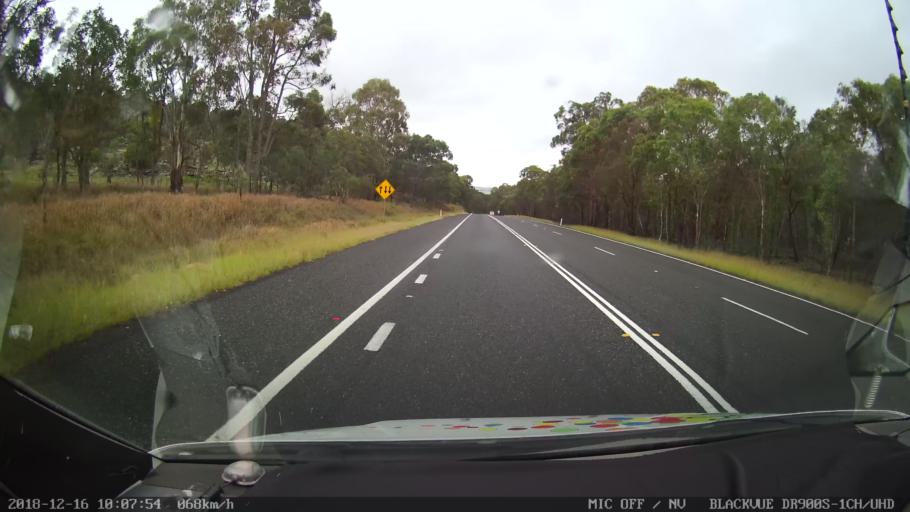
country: AU
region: New South Wales
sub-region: Glen Innes Severn
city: Glen Innes
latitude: -29.3330
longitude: 151.9002
